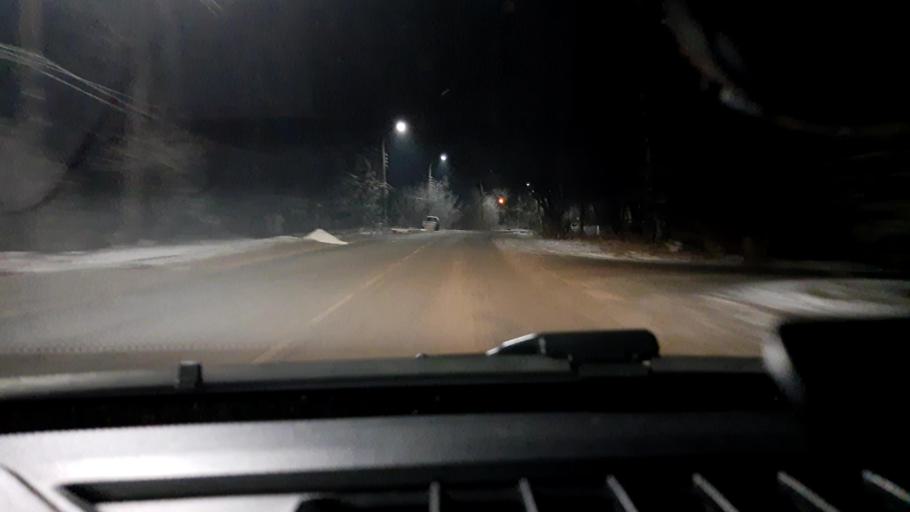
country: RU
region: Nizjnij Novgorod
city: Kstovo
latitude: 56.1765
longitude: 44.1778
